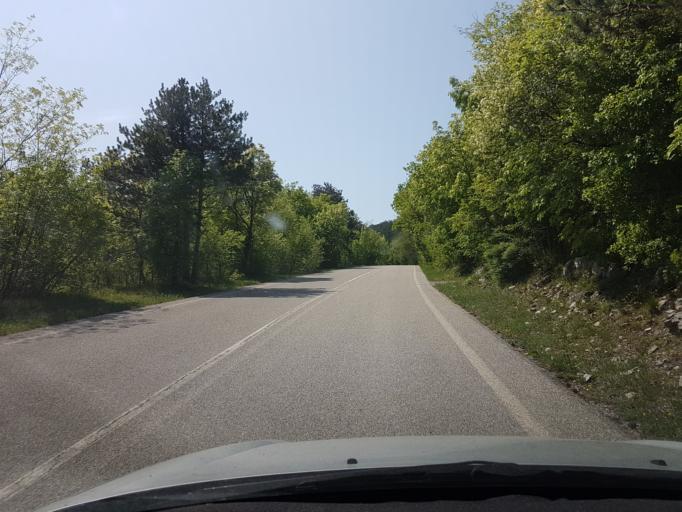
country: IT
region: Friuli Venezia Giulia
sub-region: Provincia di Trieste
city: Aurisina
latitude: 45.7758
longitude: 13.6983
